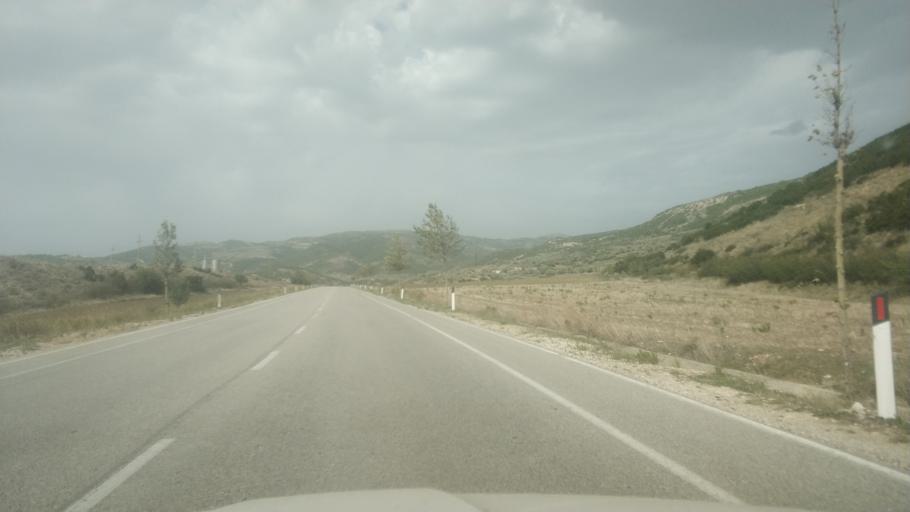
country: AL
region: Gjirokaster
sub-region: Rrethi i Tepelenes
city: Memaliaj
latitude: 40.3676
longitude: 19.9085
